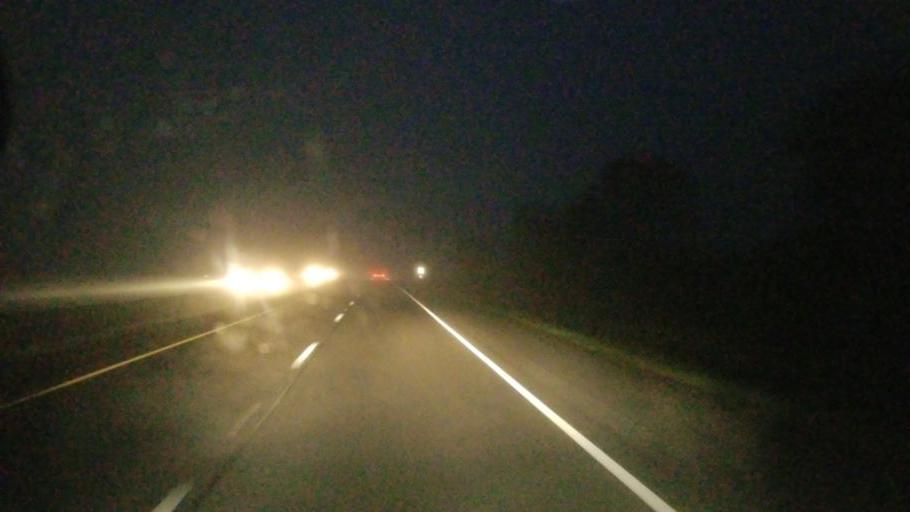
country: US
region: Ohio
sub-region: Ross County
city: Kingston
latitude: 39.4769
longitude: -82.9711
